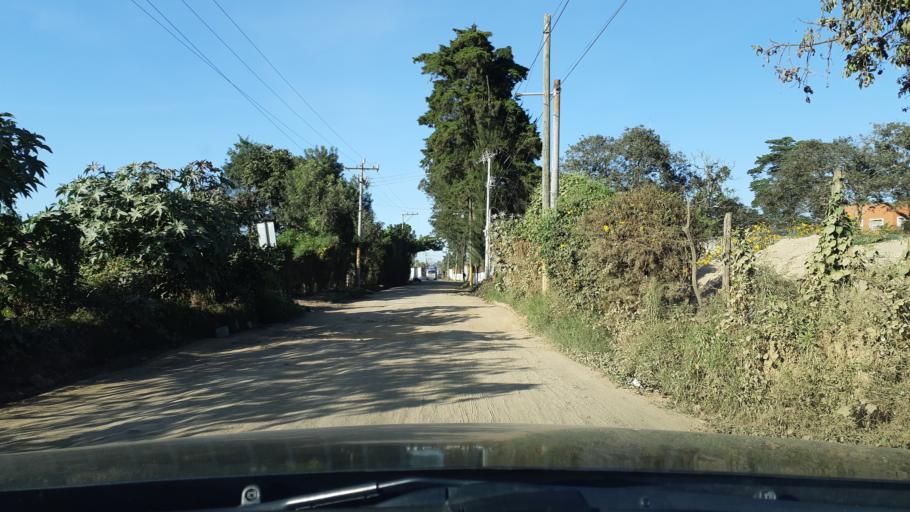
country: GT
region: Chimaltenango
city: El Tejar
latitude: 14.6386
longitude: -90.7996
